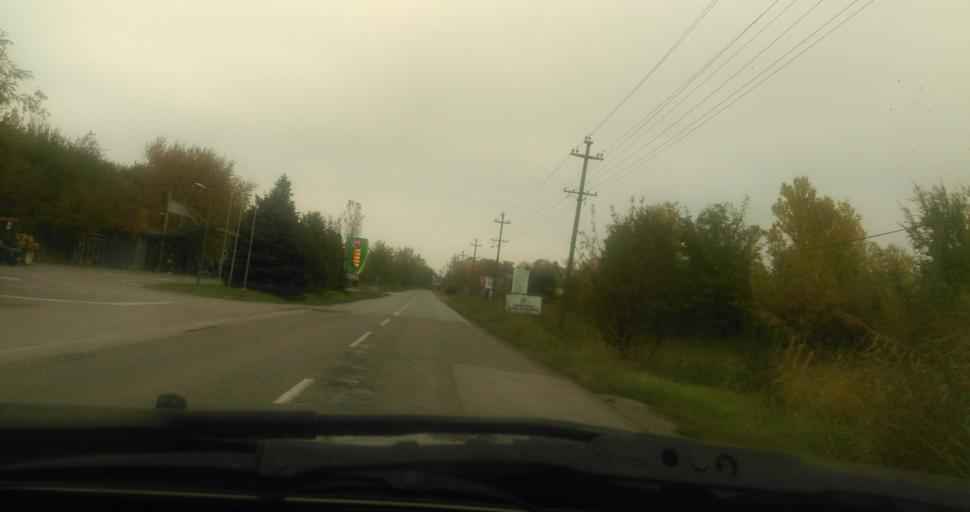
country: RS
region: Autonomna Pokrajina Vojvodina
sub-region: Juznobacki Okrug
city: Becej
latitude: 45.5965
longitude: 20.0348
